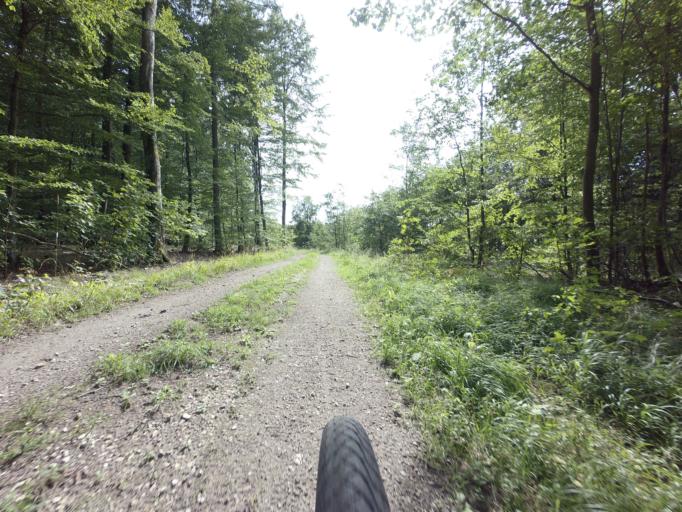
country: DK
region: Zealand
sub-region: Faxe Kommune
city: Fakse Ladeplads
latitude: 55.2370
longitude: 12.1996
